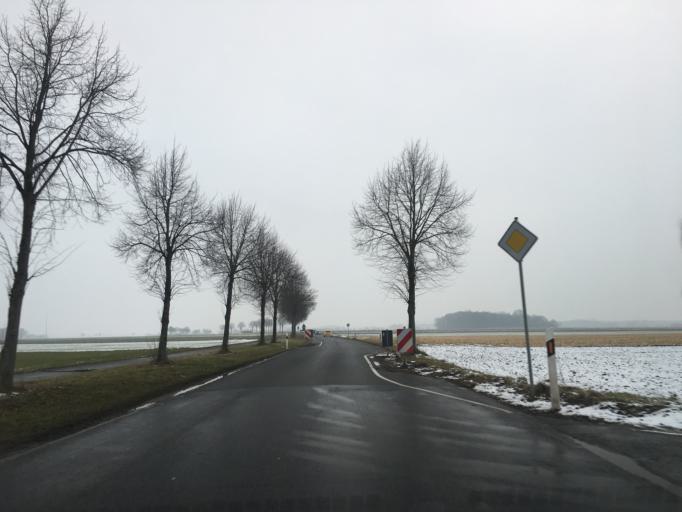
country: DE
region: North Rhine-Westphalia
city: Huckelhoven
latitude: 51.1062
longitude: 6.2387
